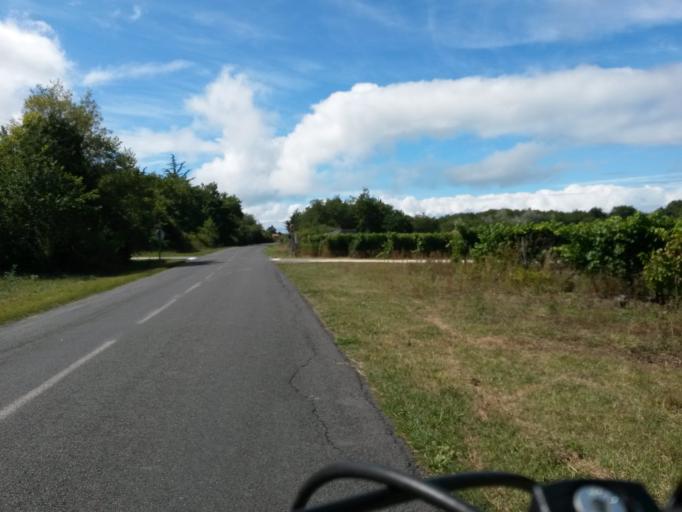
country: FR
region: Poitou-Charentes
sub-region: Departement de la Charente-Maritime
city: Dolus-d'Oleron
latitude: 45.9411
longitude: -1.3292
